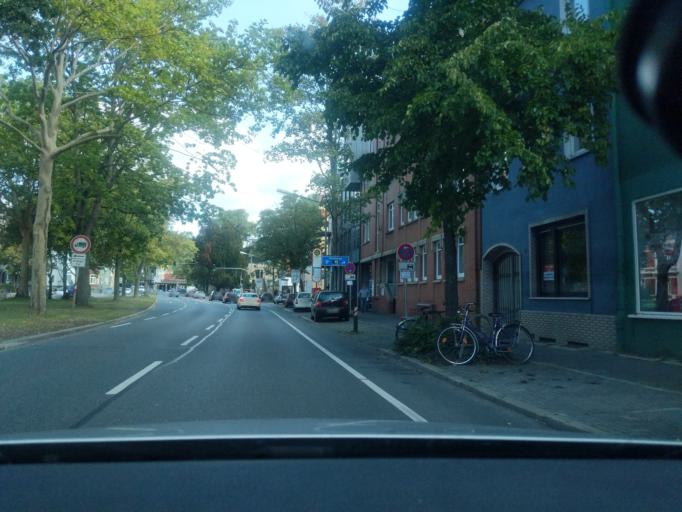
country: DE
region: Lower Saxony
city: Osnabrueck
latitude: 52.2803
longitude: 8.0411
